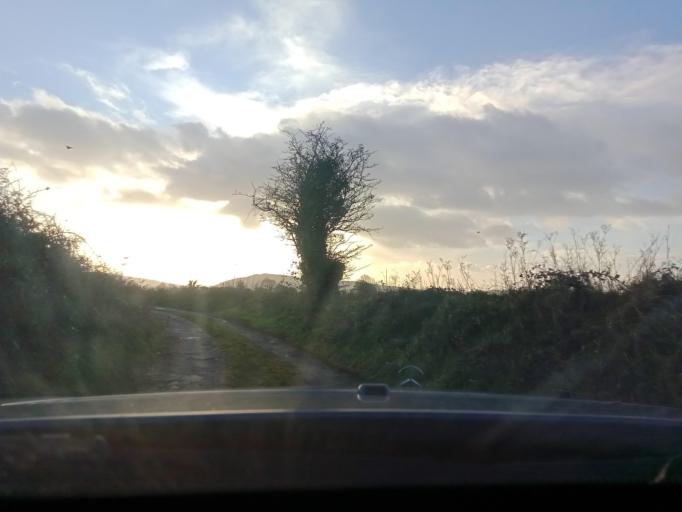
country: IE
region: Leinster
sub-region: Kilkenny
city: Callan
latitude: 52.4586
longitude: -7.4303
